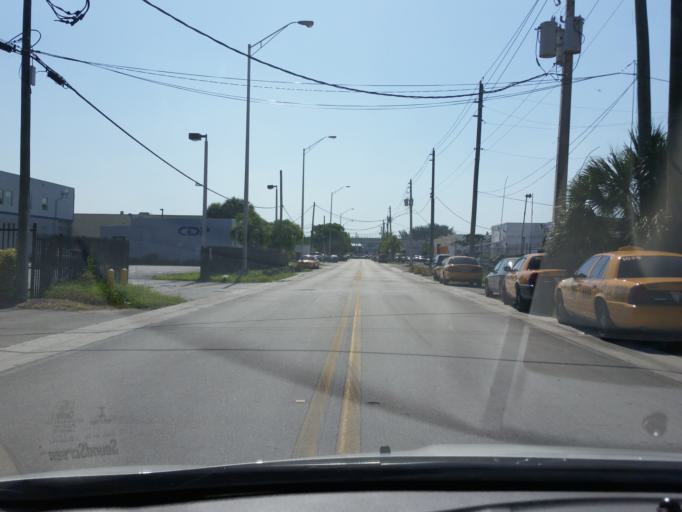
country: US
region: Florida
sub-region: Miami-Dade County
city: Brownsville
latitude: 25.7996
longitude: -80.2629
